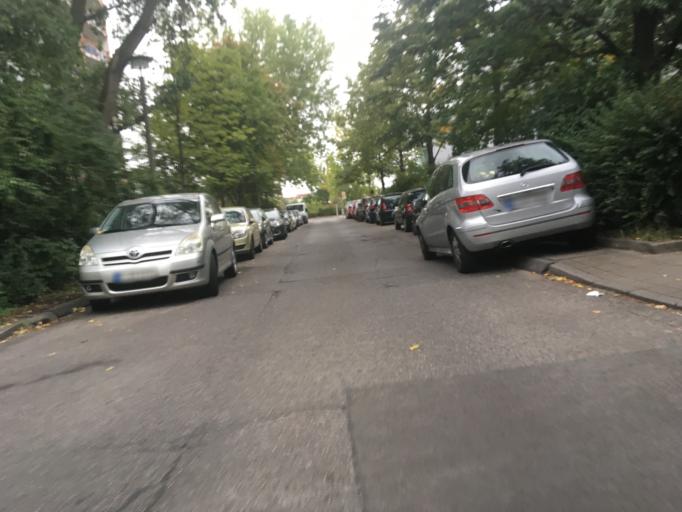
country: DE
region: Berlin
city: Fennpfuhl
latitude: 52.5252
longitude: 13.4674
